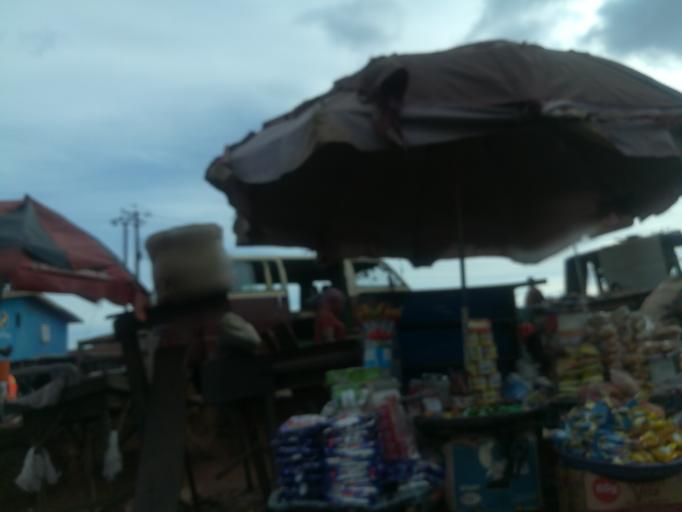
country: NG
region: Oyo
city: Ibadan
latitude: 7.3822
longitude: 3.9348
